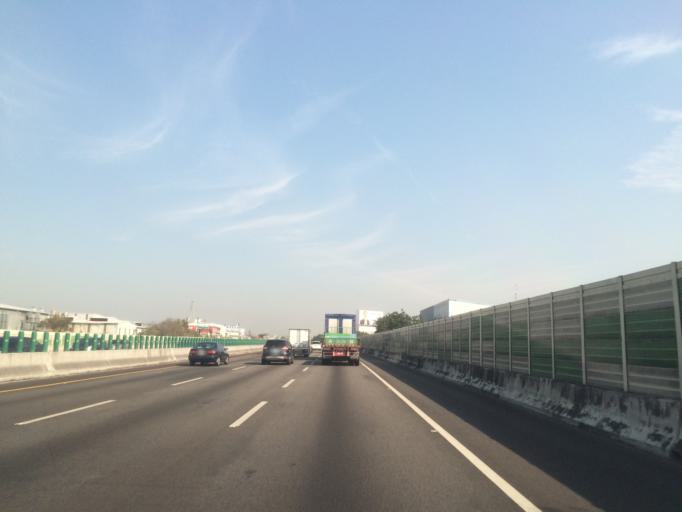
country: TW
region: Taiwan
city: Fengyuan
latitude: 24.2251
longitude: 120.6837
